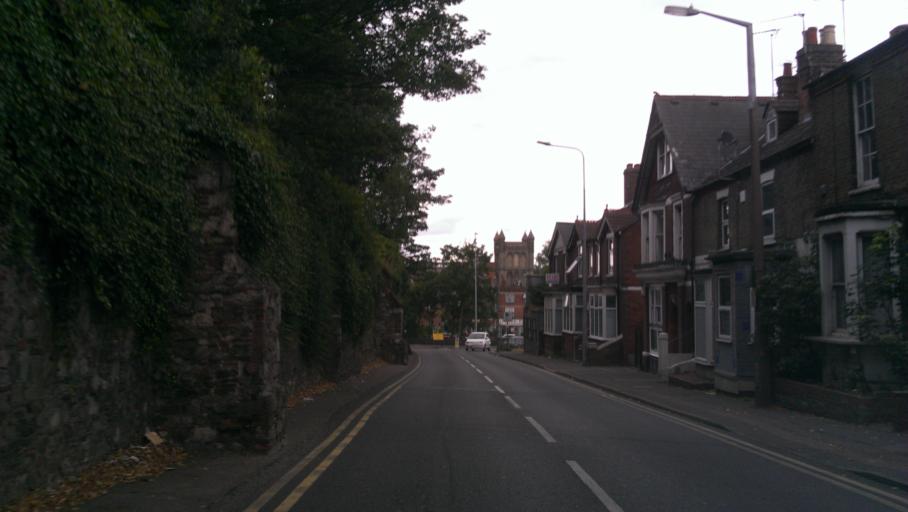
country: GB
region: England
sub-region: Essex
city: Colchester
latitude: 51.8848
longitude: 0.9035
